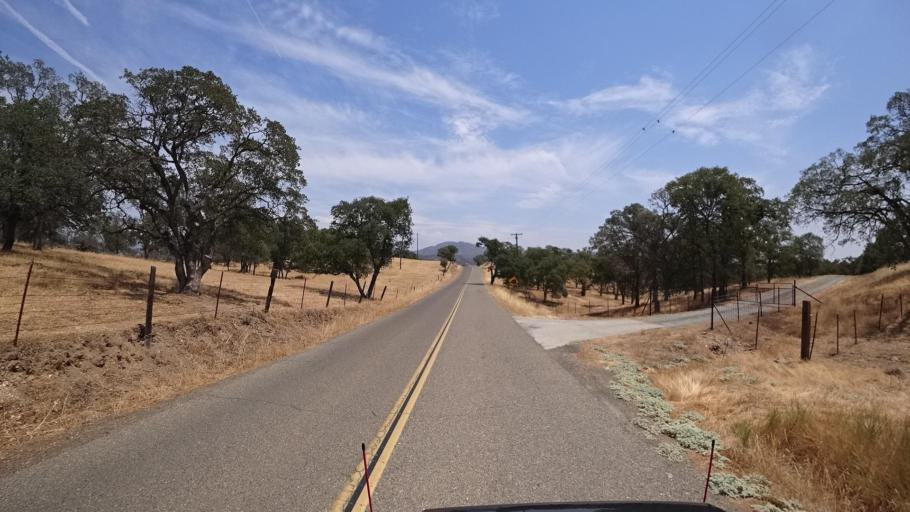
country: US
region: California
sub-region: Tuolumne County
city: Tuolumne City
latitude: 37.6444
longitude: -120.3024
